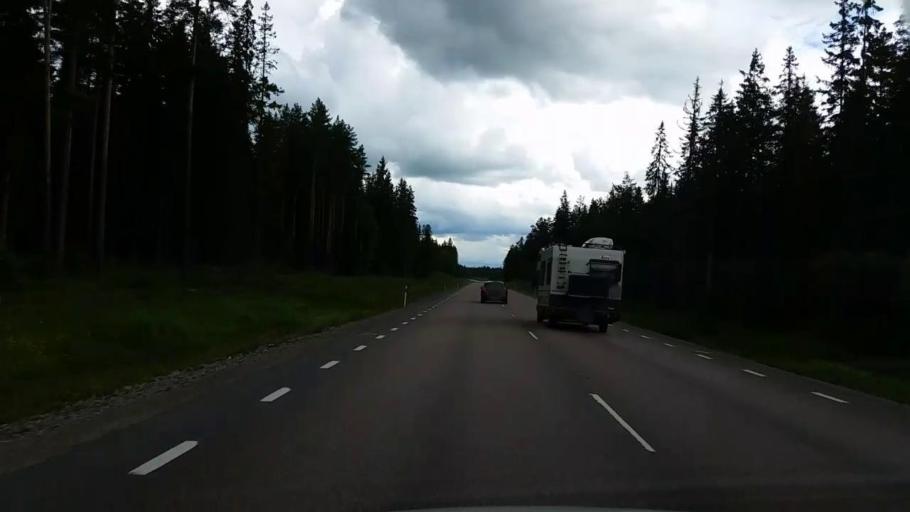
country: SE
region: Dalarna
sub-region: Avesta Kommun
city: Horndal
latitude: 60.4585
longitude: 16.4458
